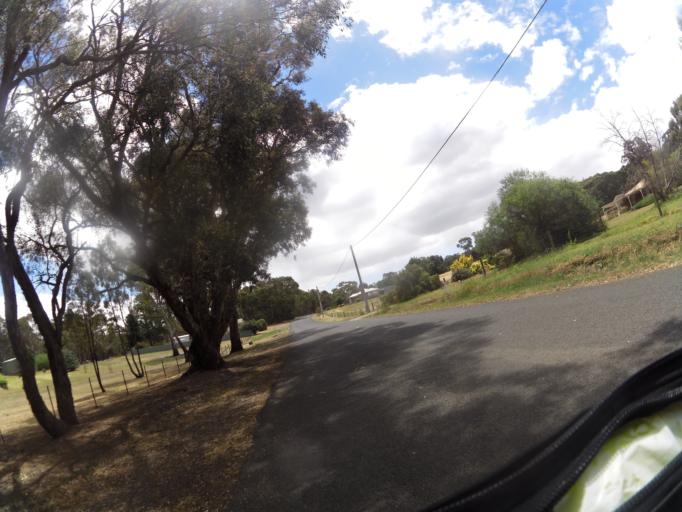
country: AU
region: Victoria
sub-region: Mount Alexander
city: Castlemaine
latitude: -37.0250
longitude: 144.2416
